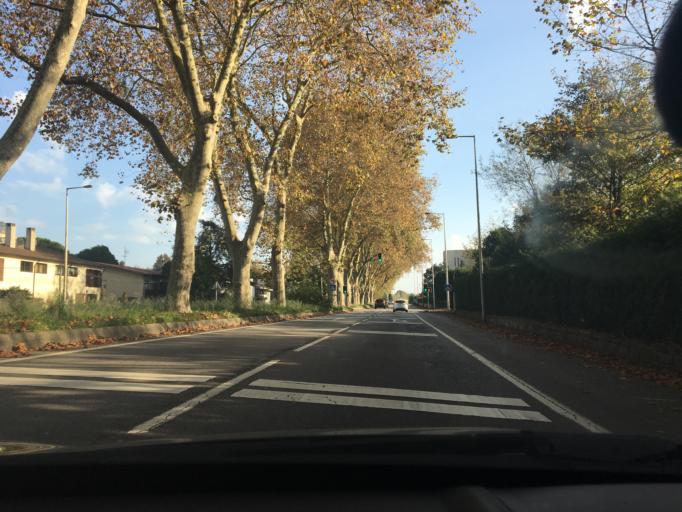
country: PT
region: Porto
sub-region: Matosinhos
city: Senhora da Hora
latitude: 41.1786
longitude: -8.6637
